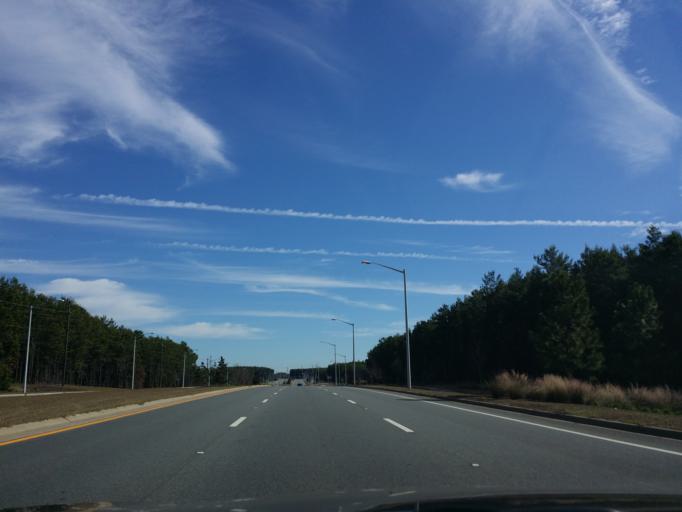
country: US
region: Florida
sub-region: Leon County
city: Woodville
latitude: 30.3755
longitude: -84.2550
